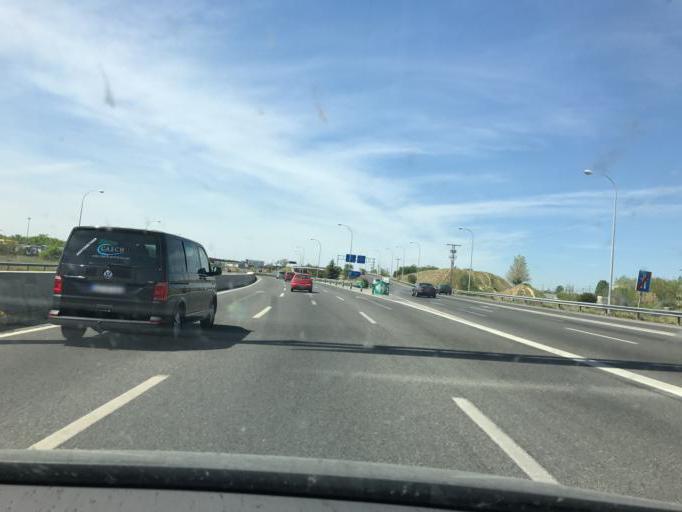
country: ES
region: Madrid
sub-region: Provincia de Madrid
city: Leganes
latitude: 40.3625
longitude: -3.7837
